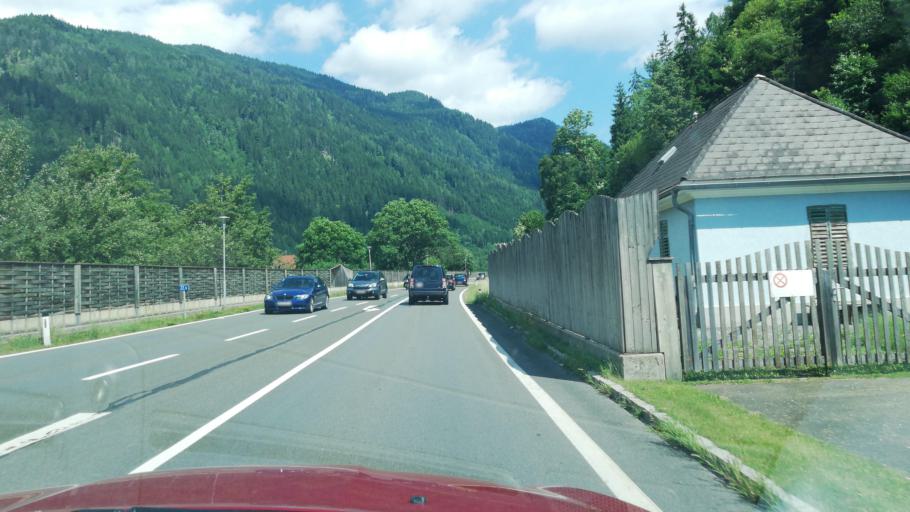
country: AT
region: Styria
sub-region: Politischer Bezirk Murau
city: Durnstein in der Steiermark
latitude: 46.9907
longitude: 14.3898
